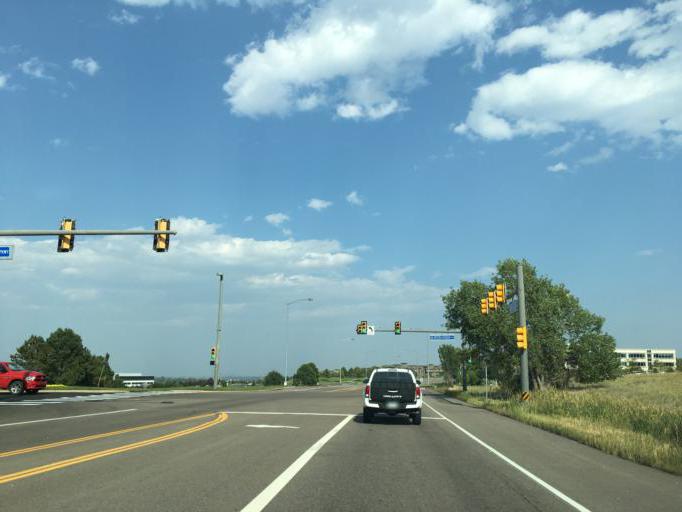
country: US
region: Colorado
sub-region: Broomfield County
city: Broomfield
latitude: 39.9166
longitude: -105.1118
